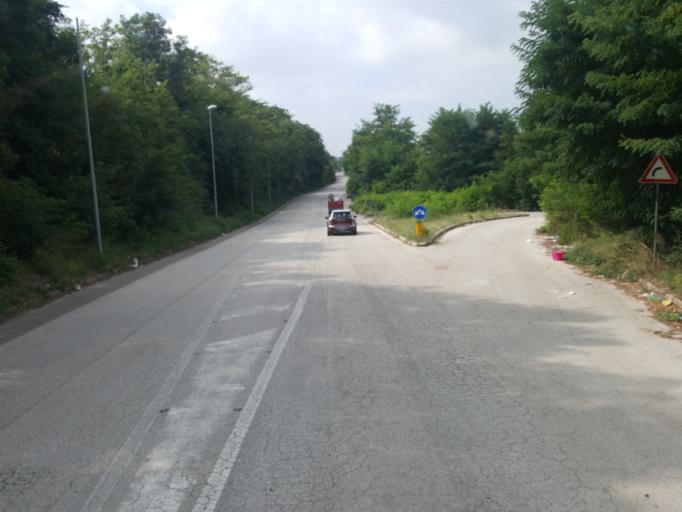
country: IT
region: Campania
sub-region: Provincia di Caserta
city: Pignataro Maggiore
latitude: 41.1778
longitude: 14.1536
